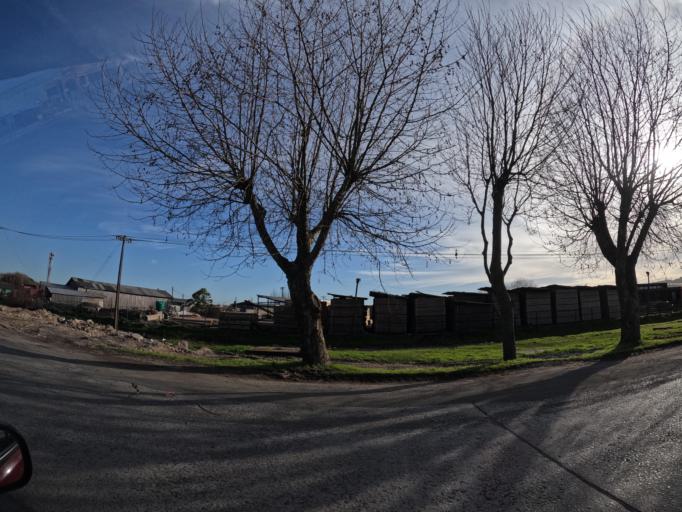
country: CL
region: Biobio
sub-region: Provincia de Concepcion
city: Concepcion
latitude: -36.7776
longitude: -73.0789
